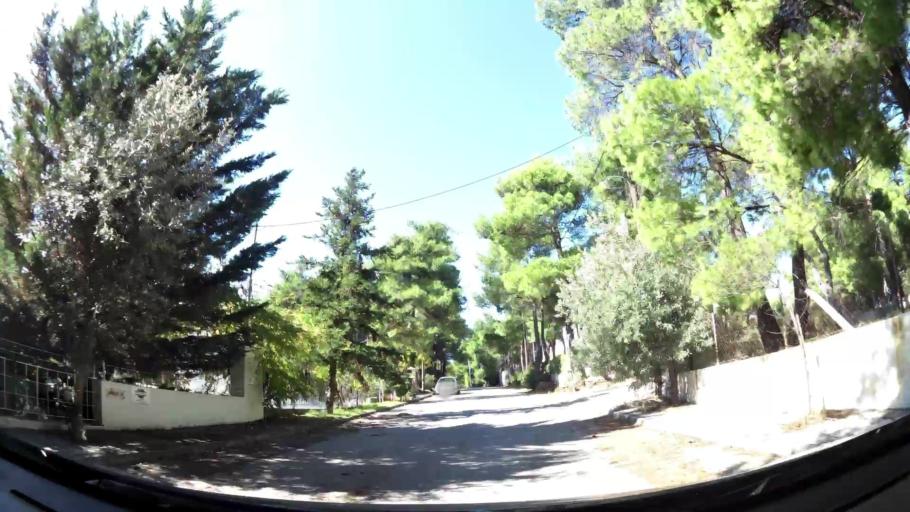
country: GR
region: Attica
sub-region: Nomarchia Anatolikis Attikis
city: Dionysos
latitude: 38.1044
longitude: 23.8818
